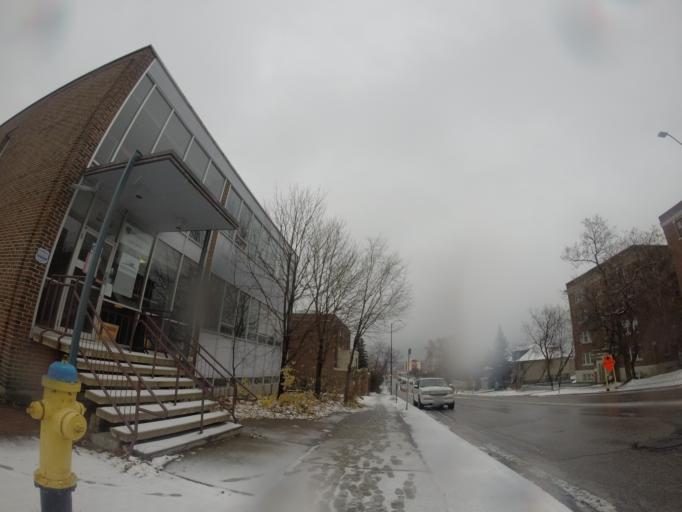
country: CA
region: Ontario
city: Greater Sudbury
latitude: 46.4932
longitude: -81.0047
